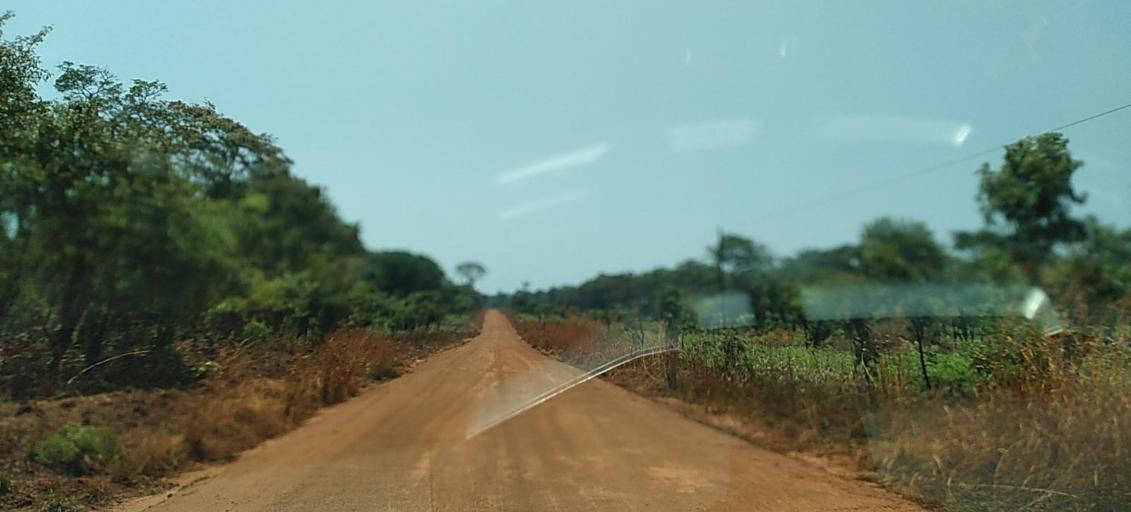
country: CD
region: Katanga
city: Kipushi
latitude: -11.9843
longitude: 26.8654
